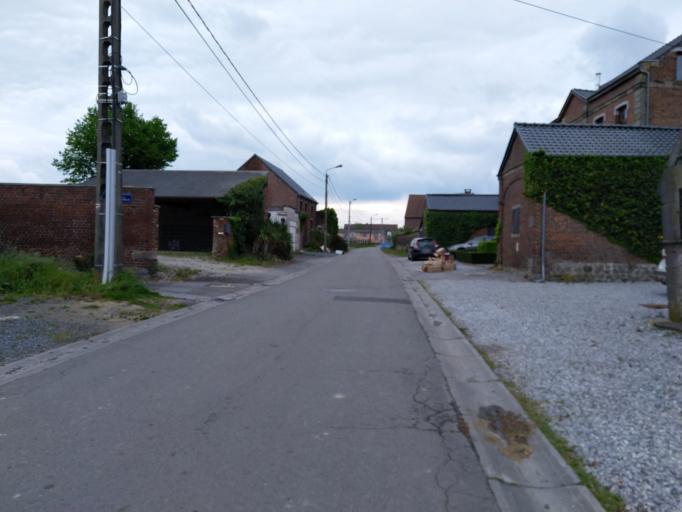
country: BE
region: Wallonia
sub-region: Province du Hainaut
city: Jurbise
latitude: 50.5309
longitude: 3.8857
